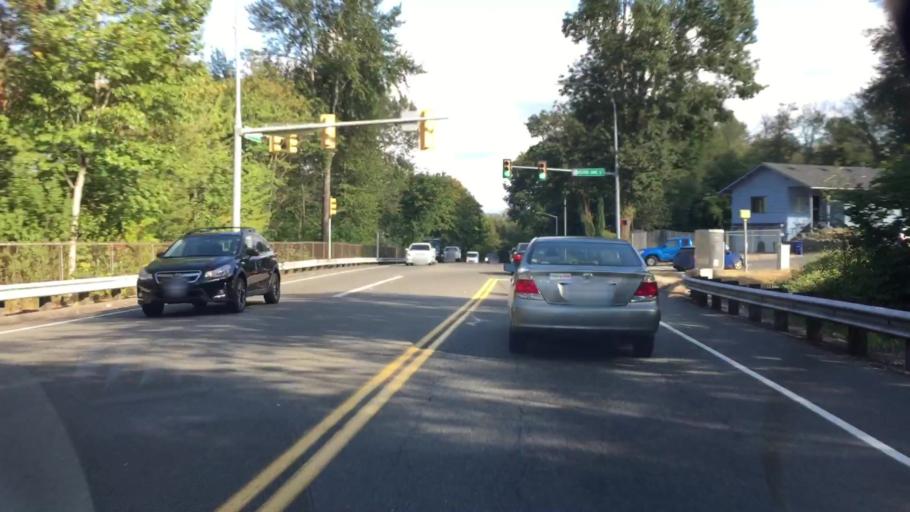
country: US
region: Washington
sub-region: King County
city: Tukwila
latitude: 47.4614
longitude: -122.2683
